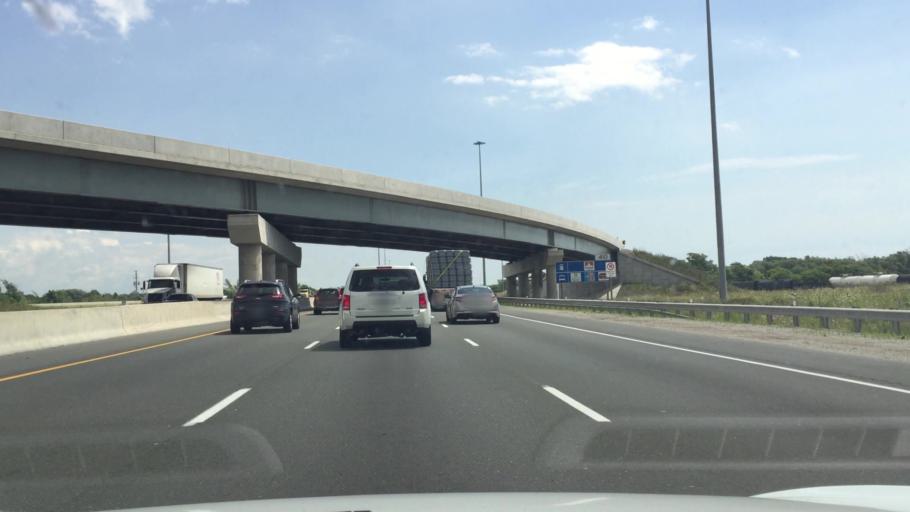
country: CA
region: Ontario
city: Ajax
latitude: 43.8664
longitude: -78.9719
